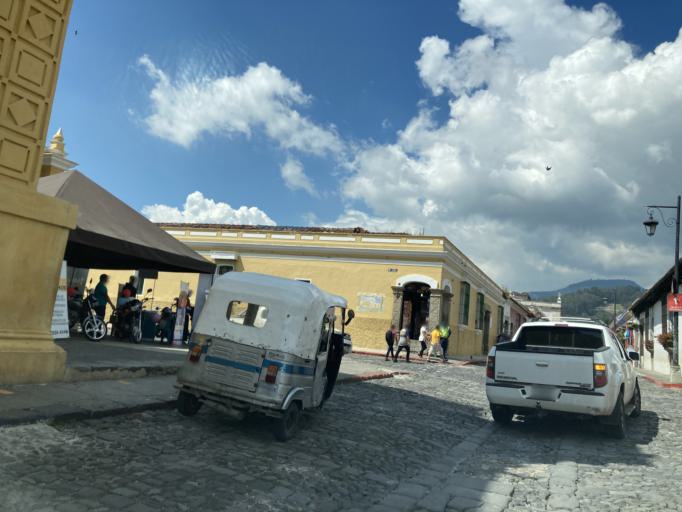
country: GT
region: Sacatepequez
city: Antigua Guatemala
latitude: 14.5552
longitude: -90.7322
